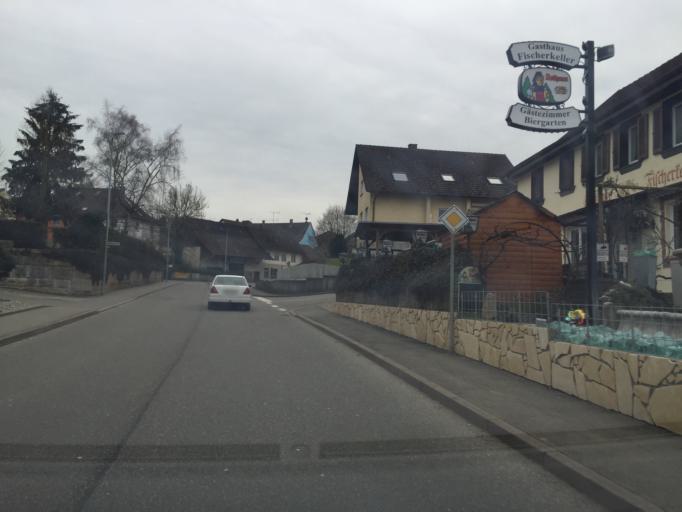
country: DE
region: Baden-Wuerttemberg
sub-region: Freiburg Region
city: Gottmadingen
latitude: 47.7234
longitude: 8.7545
